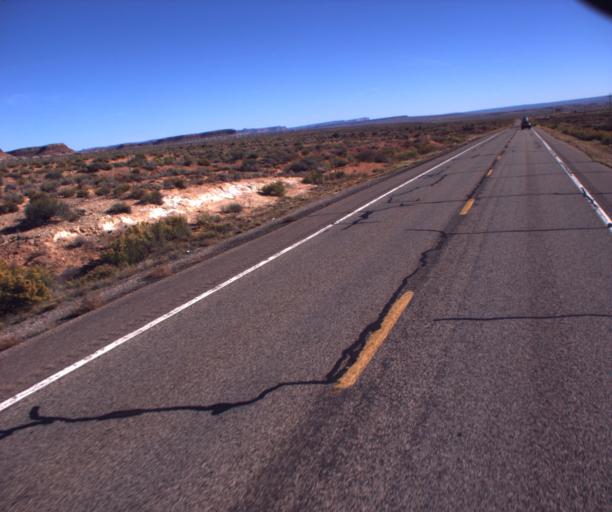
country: US
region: Arizona
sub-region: Coconino County
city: Fredonia
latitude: 36.8768
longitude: -112.6569
